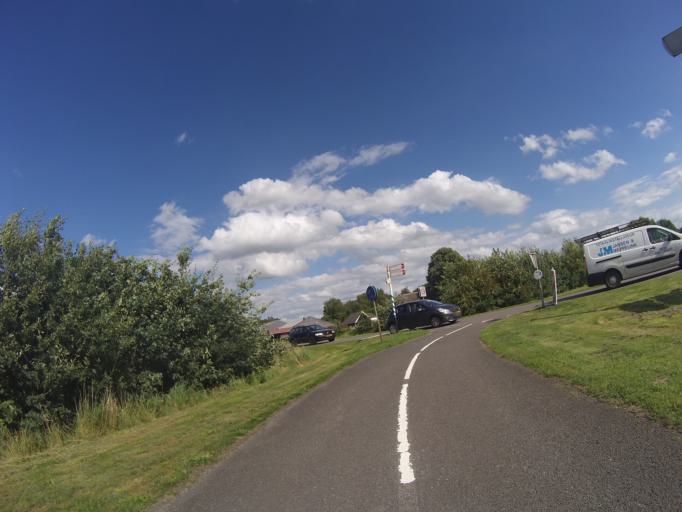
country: NL
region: Drenthe
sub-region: Gemeente Coevorden
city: Dalen
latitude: 52.7072
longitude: 6.7540
